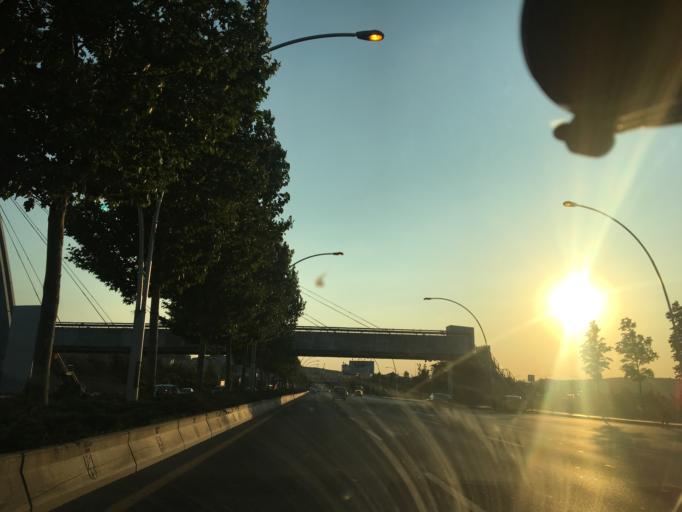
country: TR
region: Ankara
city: Batikent
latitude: 39.9060
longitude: 32.7167
